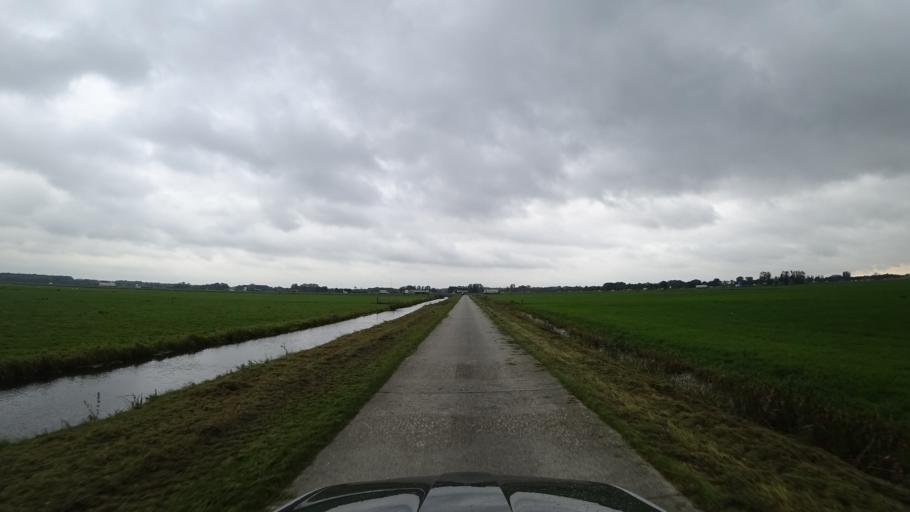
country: NL
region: Gelderland
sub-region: Gemeente Nijkerk
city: Nijkerk
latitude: 52.2534
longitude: 5.4973
